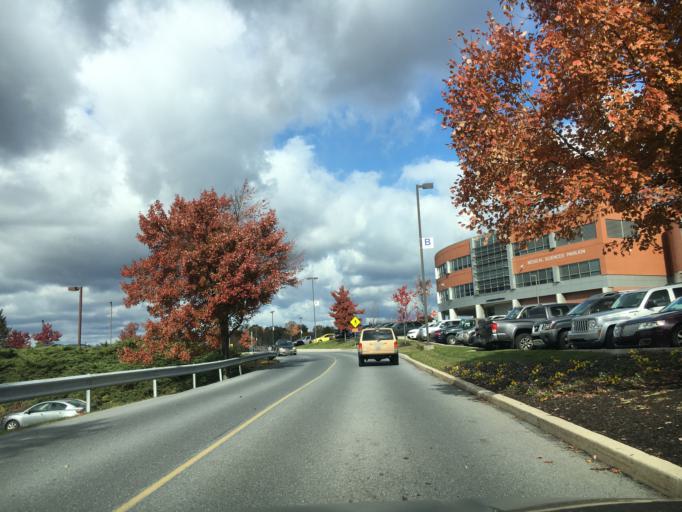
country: US
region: Pennsylvania
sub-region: Dauphin County
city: Progress
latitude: 40.2834
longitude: -76.8175
